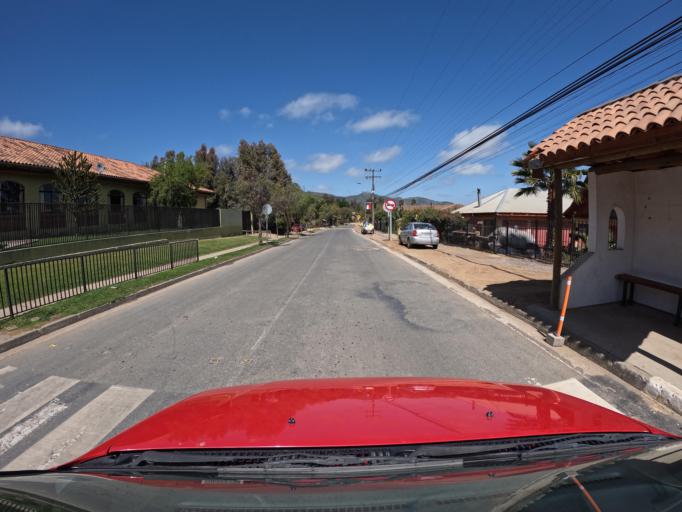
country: CL
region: O'Higgins
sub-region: Provincia de Colchagua
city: Santa Cruz
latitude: -34.7257
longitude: -71.6419
